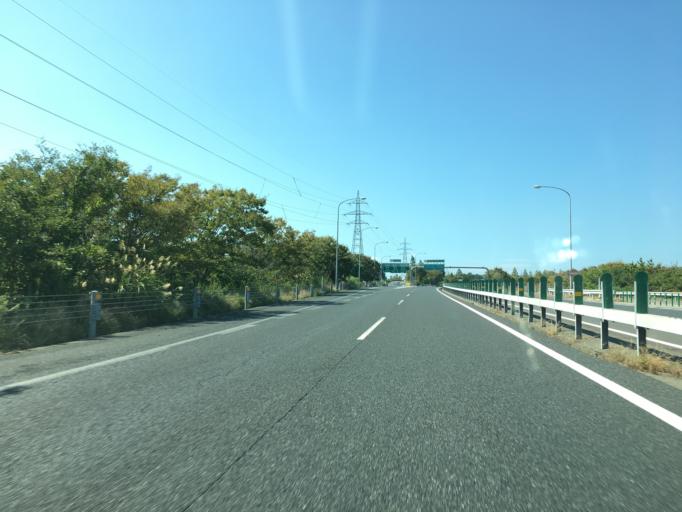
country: JP
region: Niigata
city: Niigata-shi
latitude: 37.8693
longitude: 139.0444
